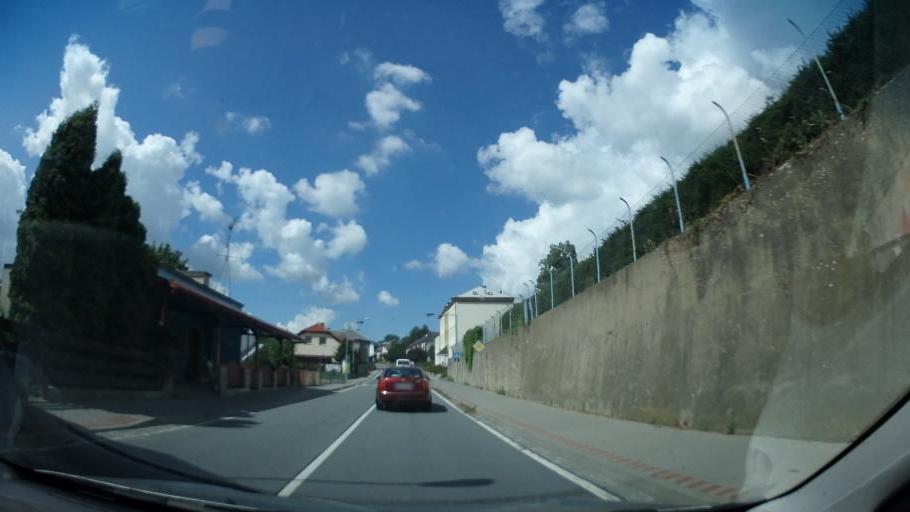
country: CZ
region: Olomoucky
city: Zabreh
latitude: 49.8824
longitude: 16.8650
